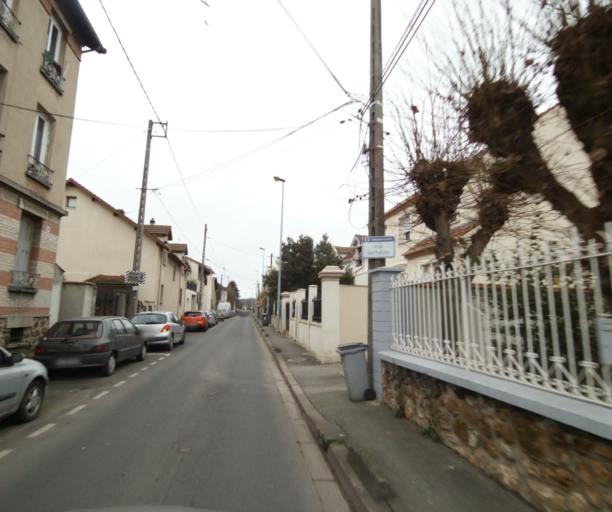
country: FR
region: Ile-de-France
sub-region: Departement du Val-de-Marne
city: Ablon-sur-Seine
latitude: 48.7260
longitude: 2.4366
